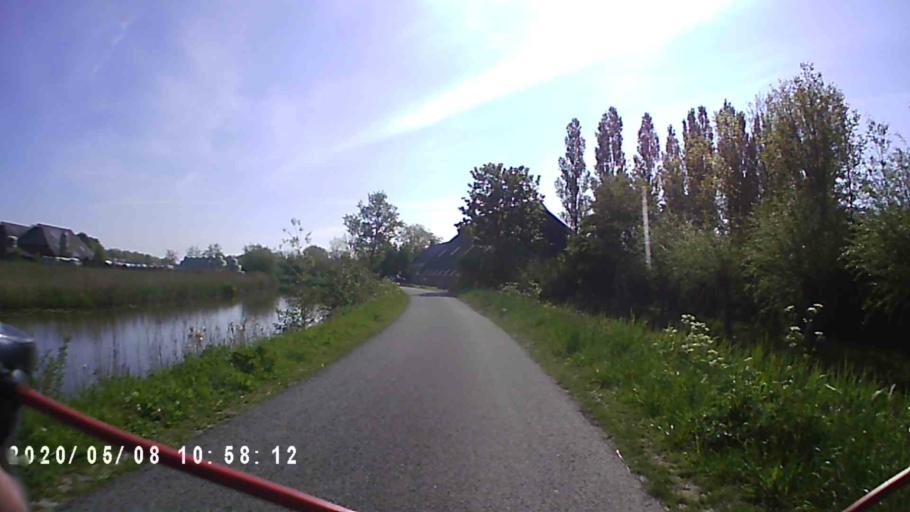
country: NL
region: Groningen
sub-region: Gemeente Bedum
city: Bedum
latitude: 53.3372
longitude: 6.6144
